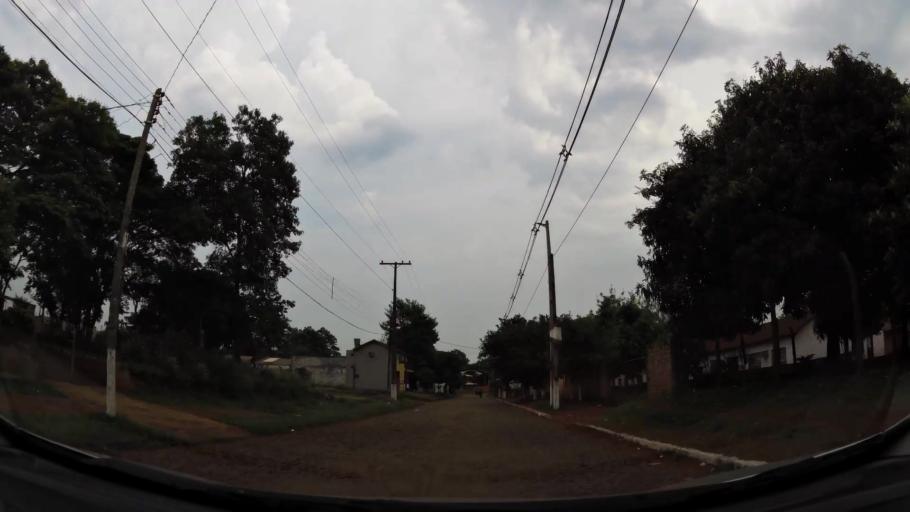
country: PY
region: Alto Parana
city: Presidente Franco
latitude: -25.5501
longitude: -54.6436
